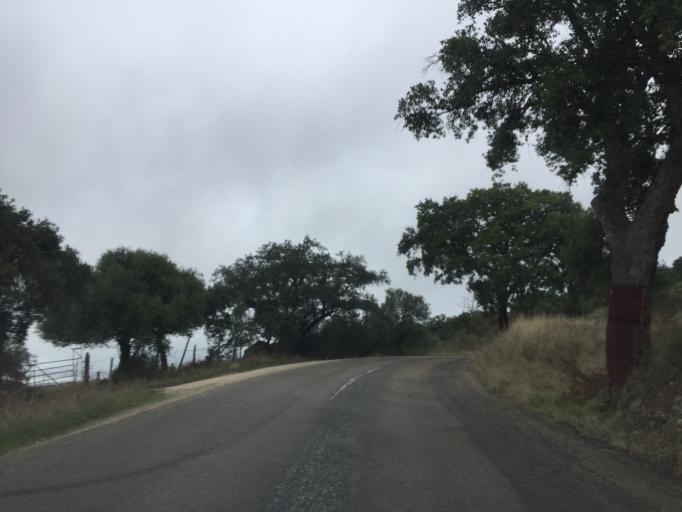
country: PT
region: Portalegre
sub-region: Alter do Chao
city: Alter do Chao
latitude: 39.2324
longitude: -7.6528
